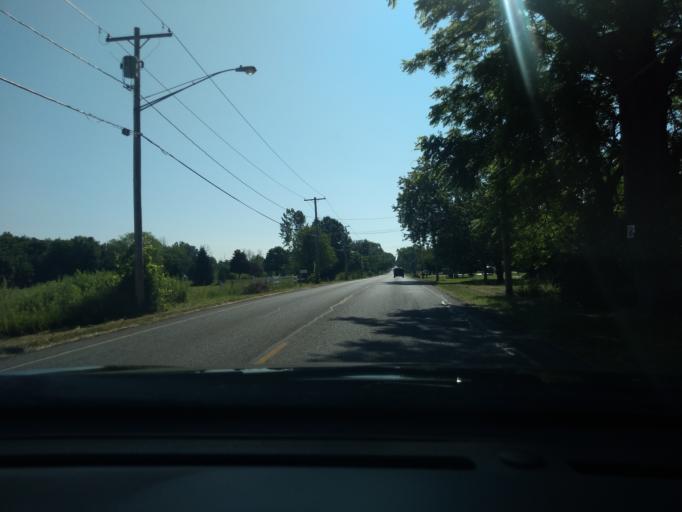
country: US
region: New York
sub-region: Erie County
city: Orchard Park
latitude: 42.7892
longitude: -78.7221
